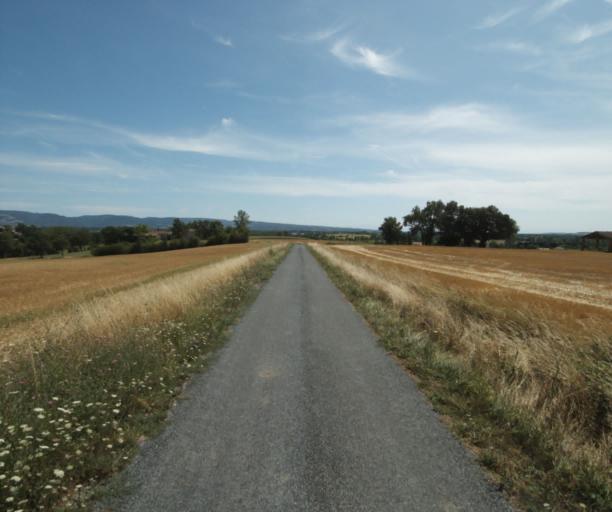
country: FR
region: Midi-Pyrenees
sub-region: Departement du Tarn
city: Puylaurens
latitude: 43.5306
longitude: 2.0030
